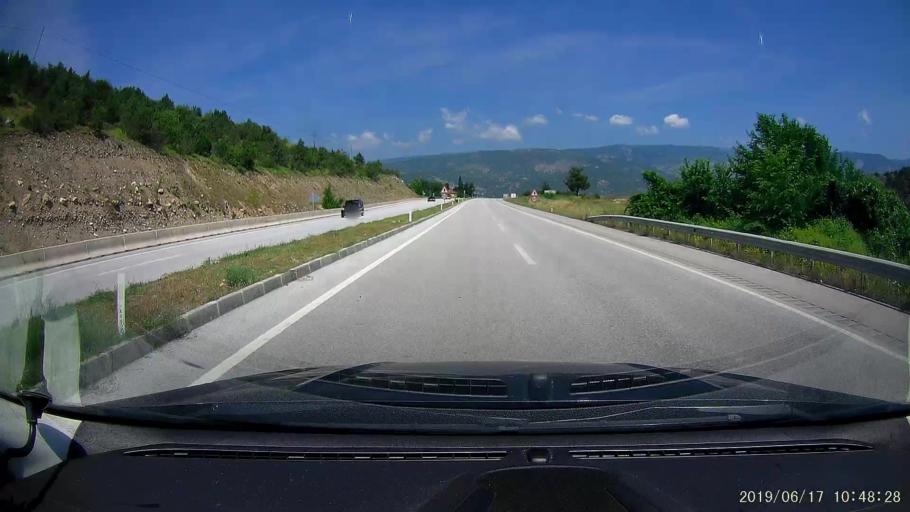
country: TR
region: Corum
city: Hacihamza
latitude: 41.0885
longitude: 34.4282
